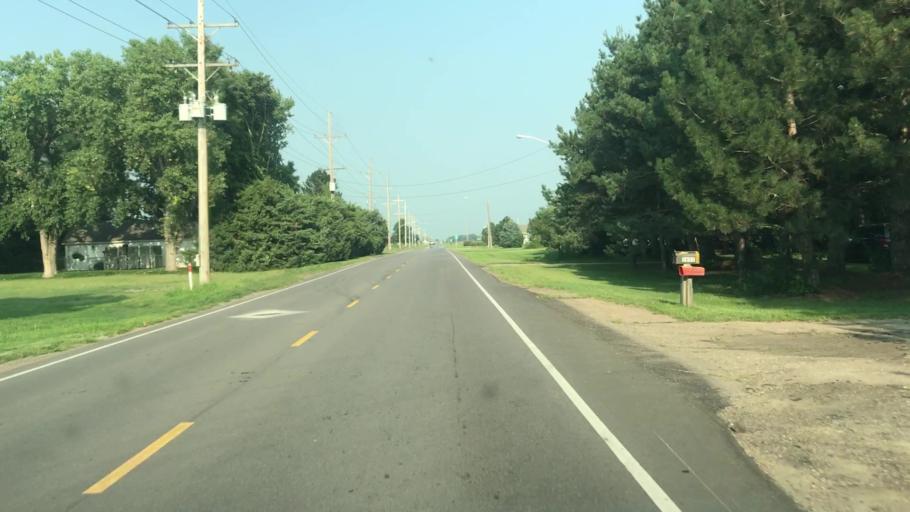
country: US
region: Nebraska
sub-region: Hall County
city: Grand Island
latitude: 40.9455
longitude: -98.3259
